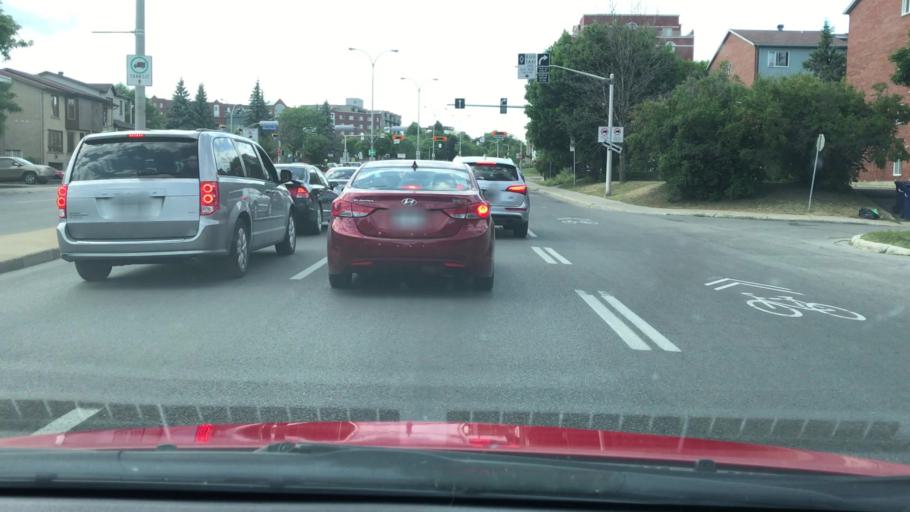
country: CA
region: Quebec
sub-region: Laval
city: Laval
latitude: 45.5434
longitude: -73.7382
